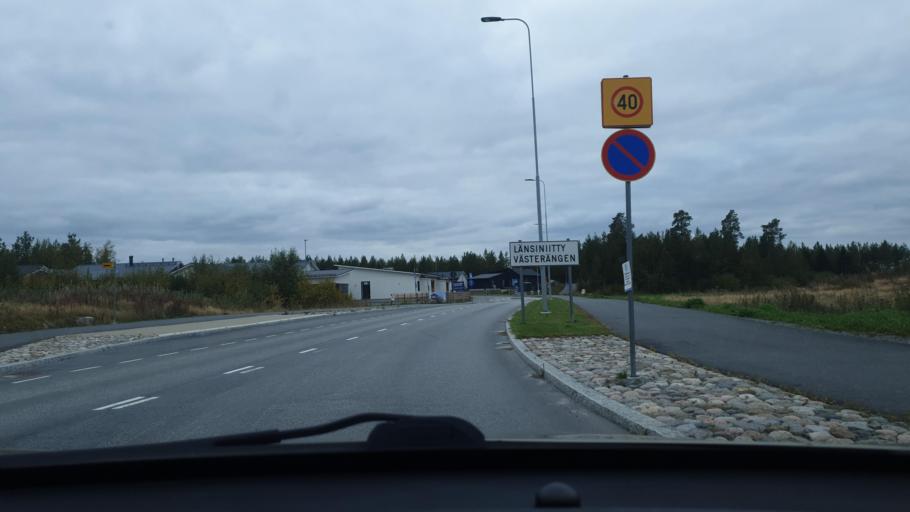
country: FI
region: Ostrobothnia
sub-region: Vaasa
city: Korsholm
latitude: 63.1292
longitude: 21.6597
